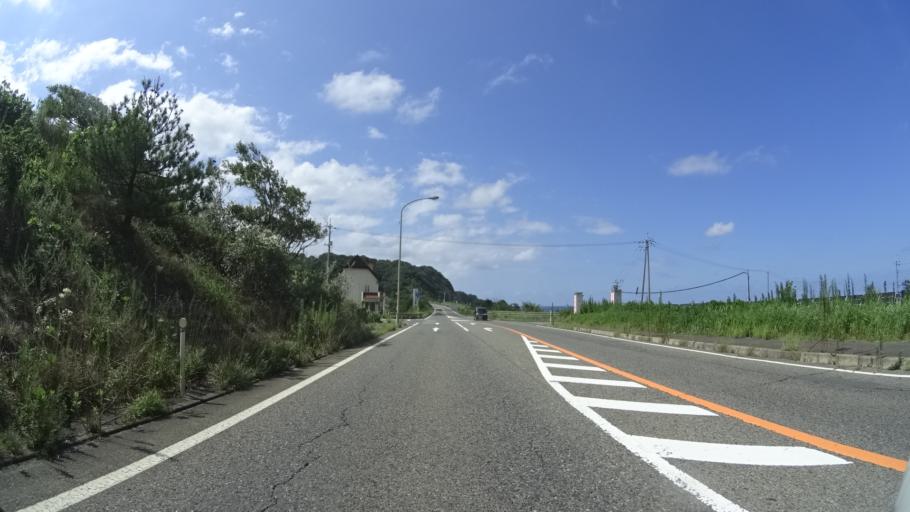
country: JP
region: Tottori
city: Tottori
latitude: 35.5222
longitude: 134.0982
